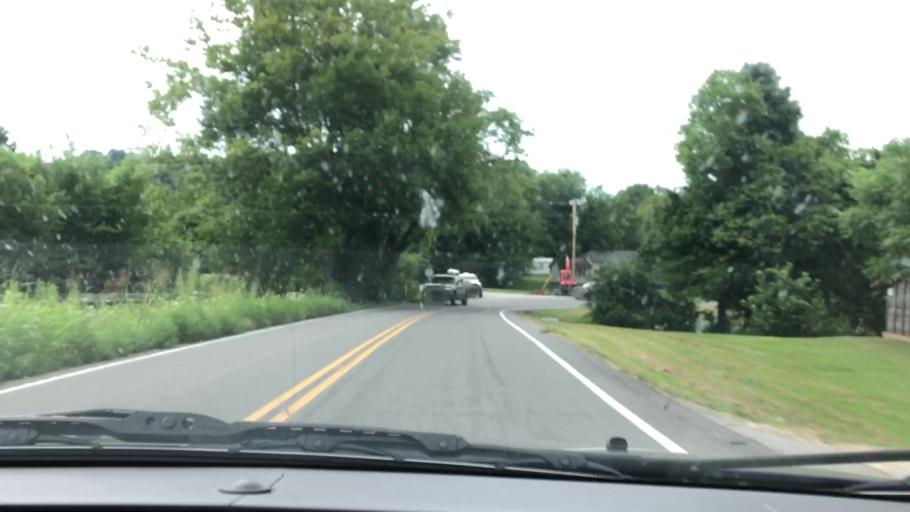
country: US
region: Tennessee
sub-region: Maury County
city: Spring Hill
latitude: 35.8021
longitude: -86.9992
